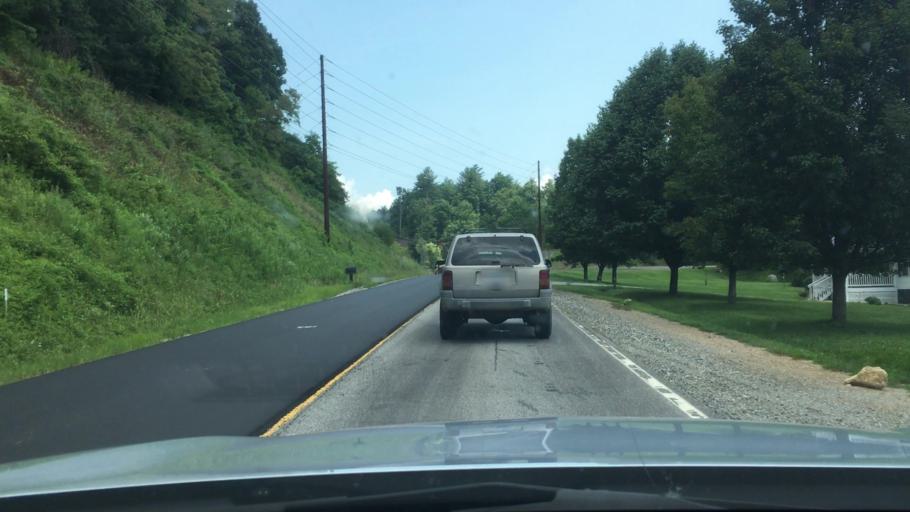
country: US
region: North Carolina
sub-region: Madison County
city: Marshall
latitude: 35.8866
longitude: -82.7427
